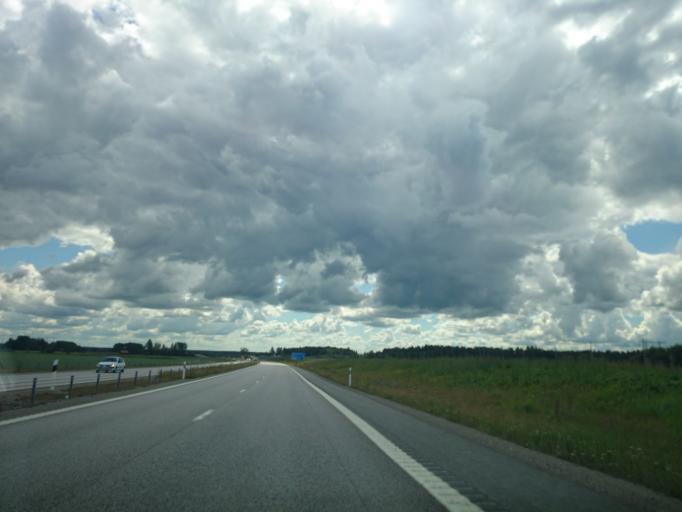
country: SE
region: Uppsala
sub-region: Tierps Kommun
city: Tierp
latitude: 60.3486
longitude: 17.4754
